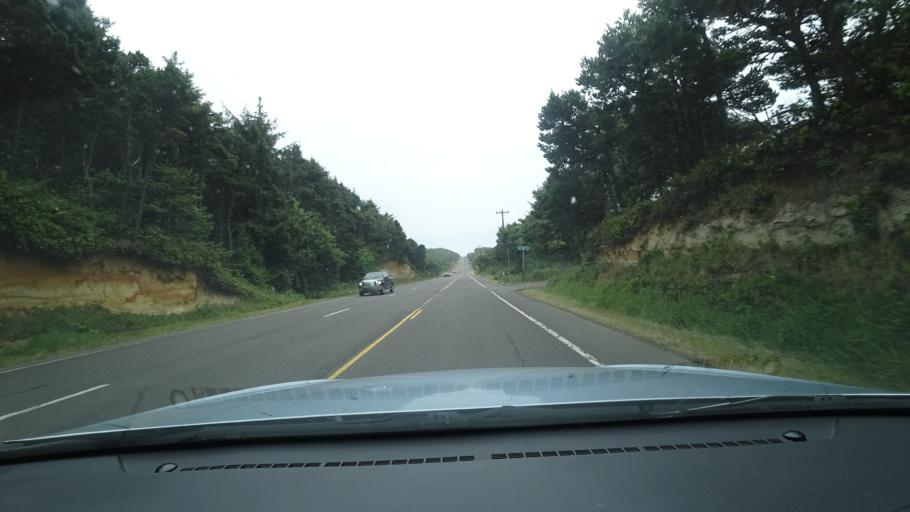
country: US
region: Oregon
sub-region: Lincoln County
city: Newport
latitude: 44.5664
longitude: -124.0688
